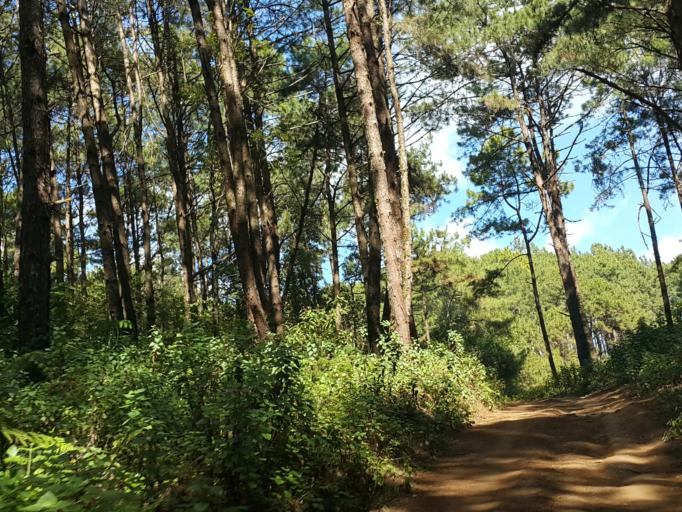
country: TH
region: Chiang Mai
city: Wiang Haeng
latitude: 19.5437
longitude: 98.8154
